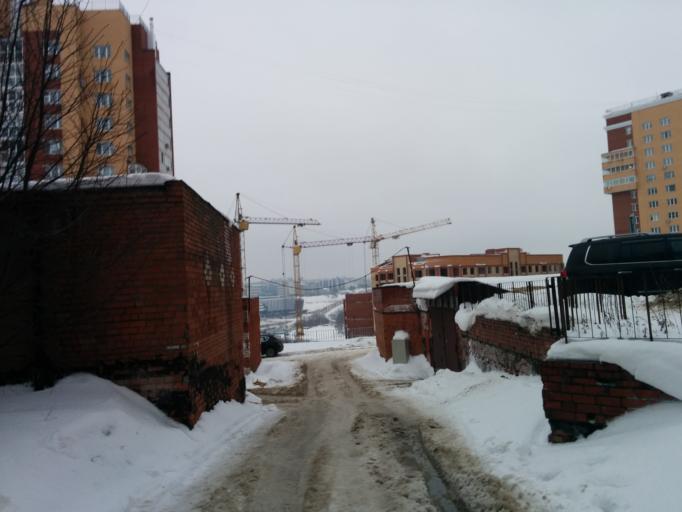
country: RU
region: Chuvashia
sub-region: Cheboksarskiy Rayon
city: Cheboksary
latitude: 56.1431
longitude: 47.2300
